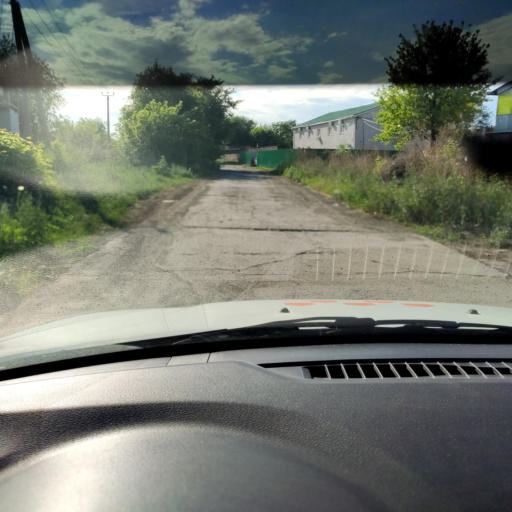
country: RU
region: Samara
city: Tol'yatti
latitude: 53.5685
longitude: 49.4698
